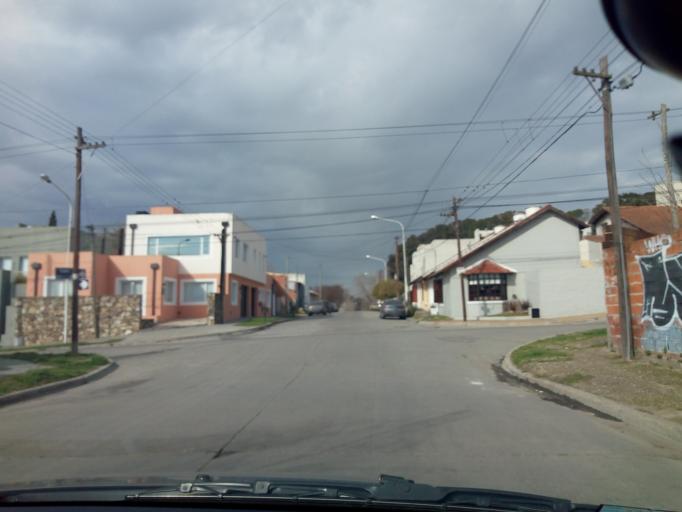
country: AR
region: Buenos Aires
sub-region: Partido de Tandil
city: Tandil
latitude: -37.3380
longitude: -59.1329
